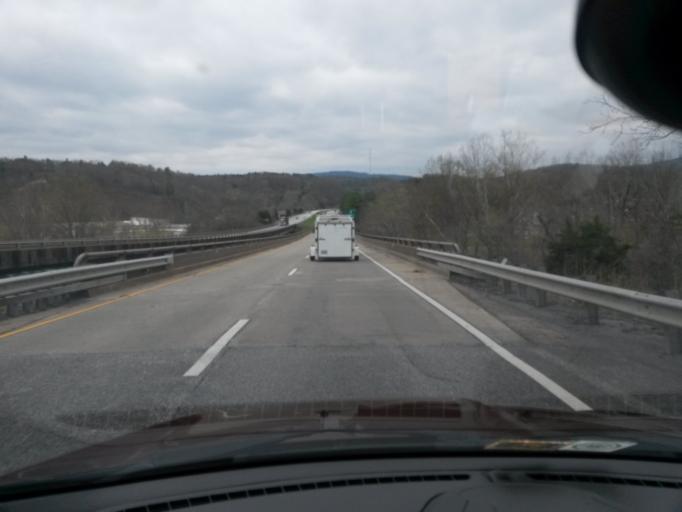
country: US
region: Virginia
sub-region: City of Covington
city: Fairlawn
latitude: 37.7722
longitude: -79.9863
